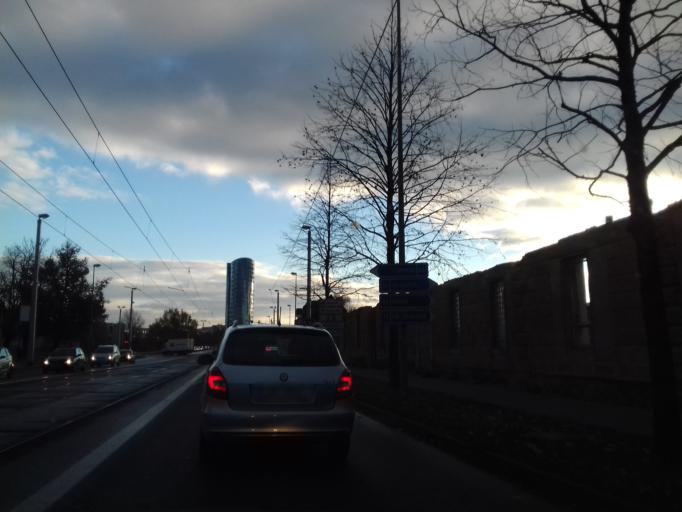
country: CZ
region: Olomoucky
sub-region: Okres Olomouc
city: Olomouc
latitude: 49.5890
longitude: 17.2588
